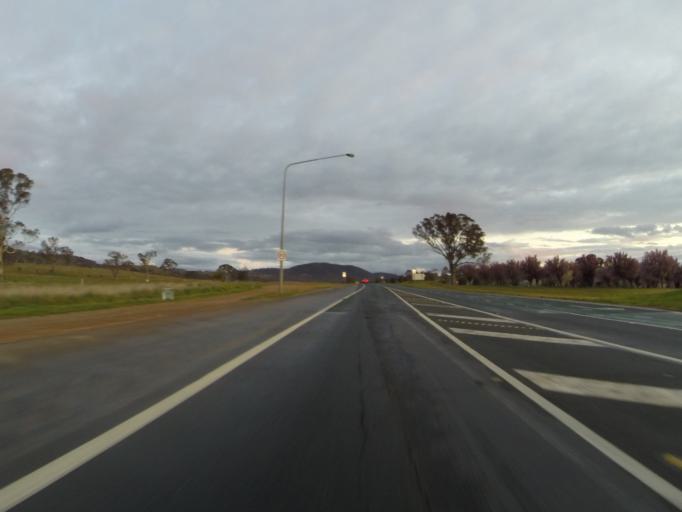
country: AU
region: Australian Capital Territory
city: Kaleen
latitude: -35.1946
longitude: 149.1618
